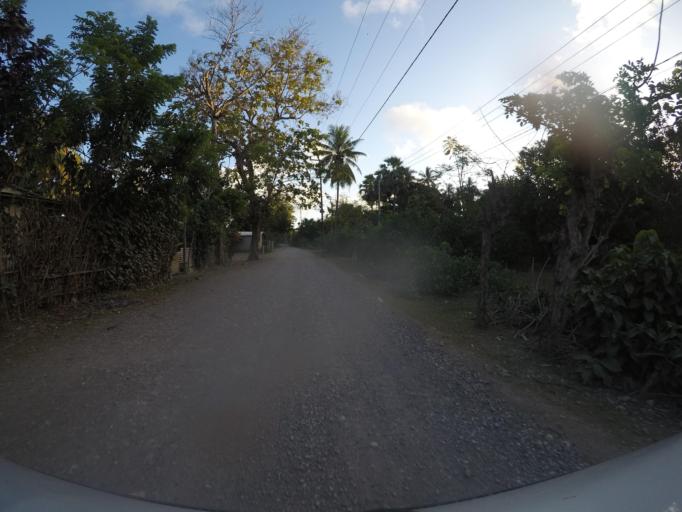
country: TL
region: Baucau
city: Venilale
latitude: -8.7433
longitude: 126.7144
